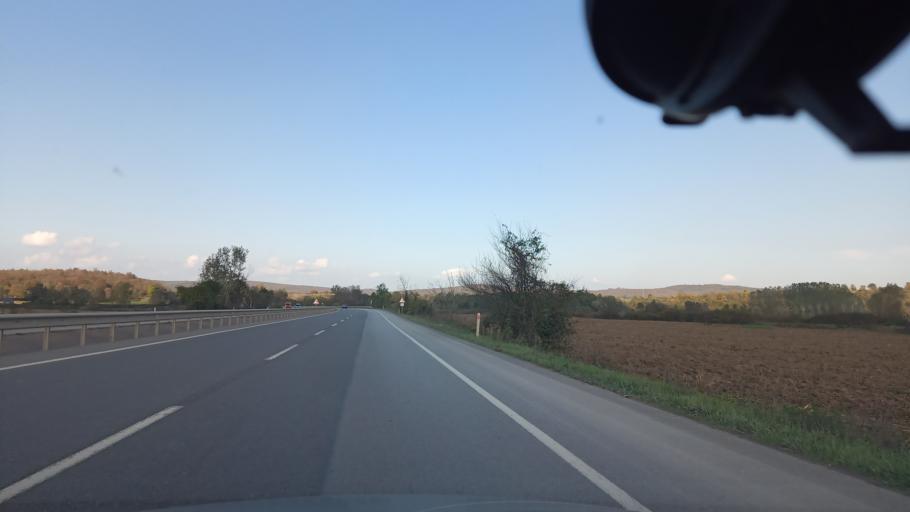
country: TR
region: Sakarya
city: Sogutlu
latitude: 40.8547
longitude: 30.4920
